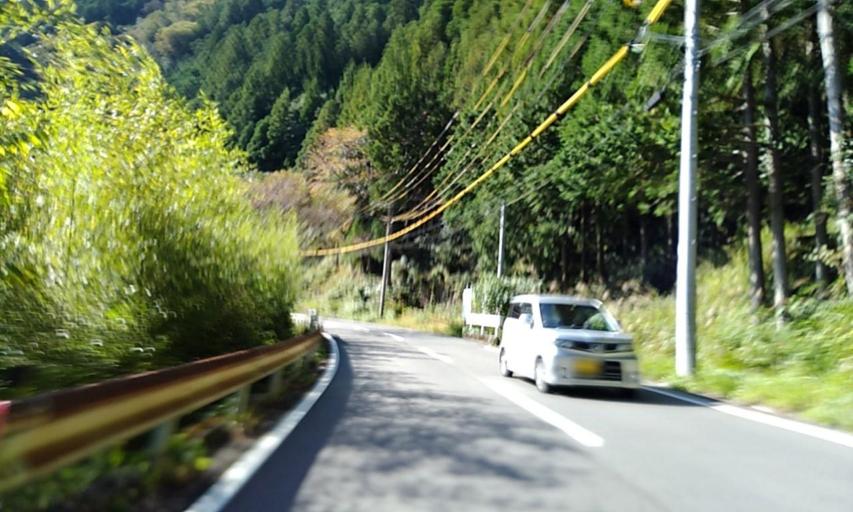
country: JP
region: Wakayama
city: Kainan
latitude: 34.0609
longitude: 135.3508
